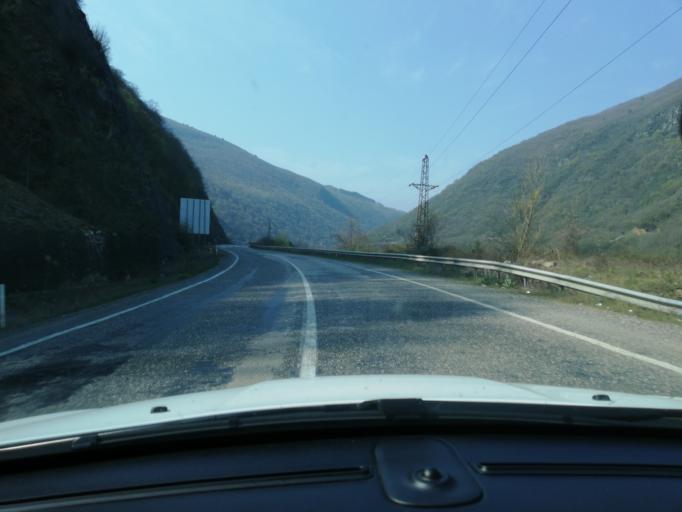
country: TR
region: Karabuk
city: Yenice
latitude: 41.2081
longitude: 32.3600
